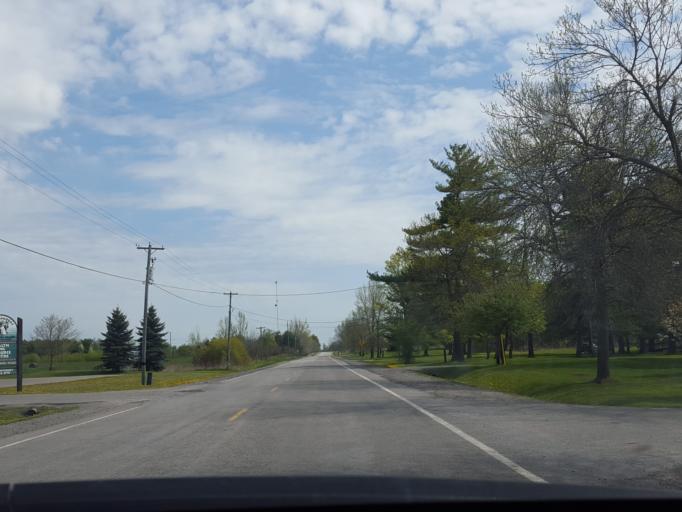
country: CA
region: Ontario
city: Uxbridge
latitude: 44.1940
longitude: -78.8810
